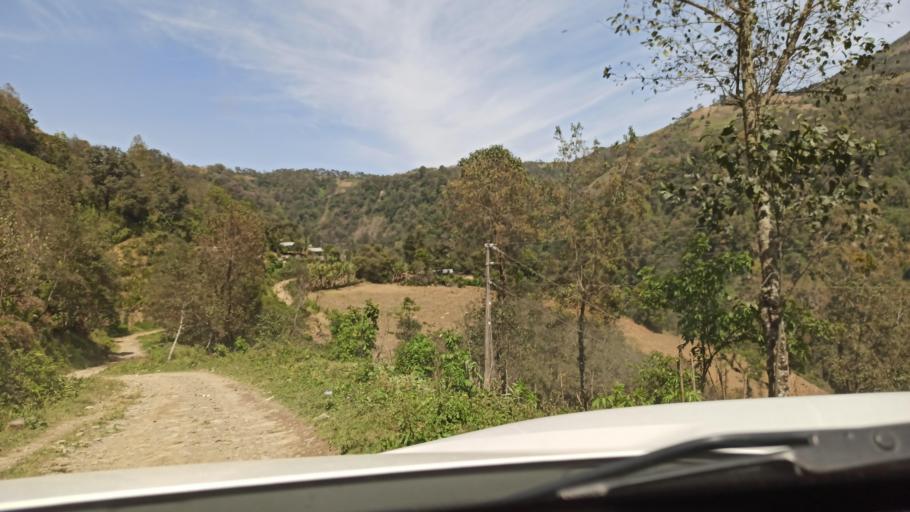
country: MX
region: Veracruz
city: Xocotla
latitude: 18.9859
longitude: -97.0990
